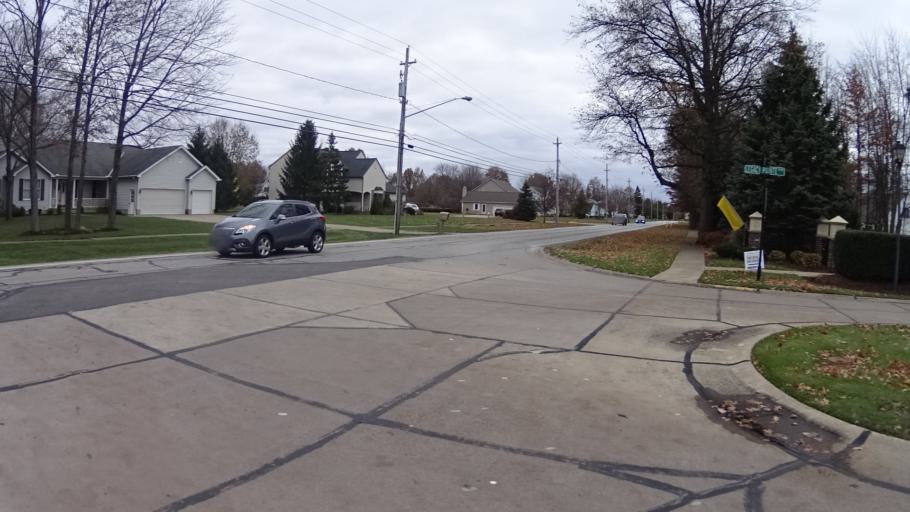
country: US
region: Ohio
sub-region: Lorain County
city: Avon Lake
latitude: 41.4878
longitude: -81.9976
